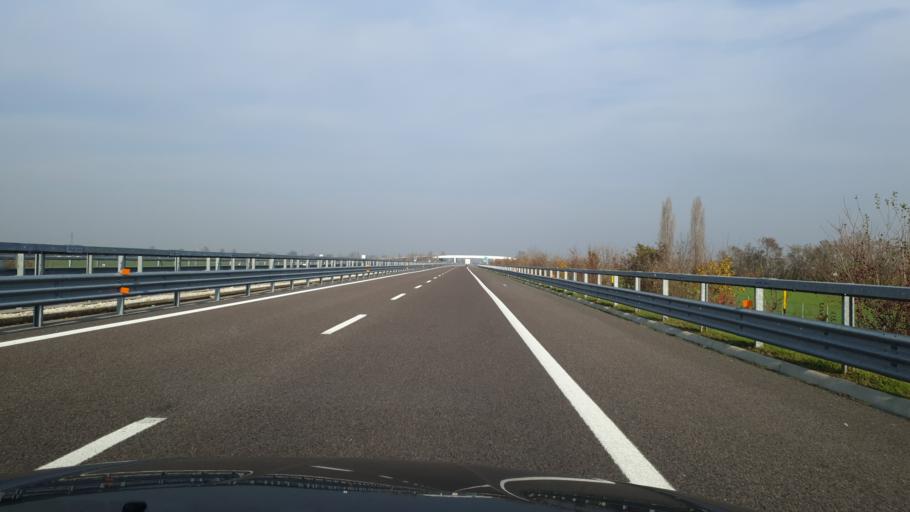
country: IT
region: Veneto
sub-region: Provincia di Padova
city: Piacenza d'Adige
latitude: 45.1397
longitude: 11.5312
